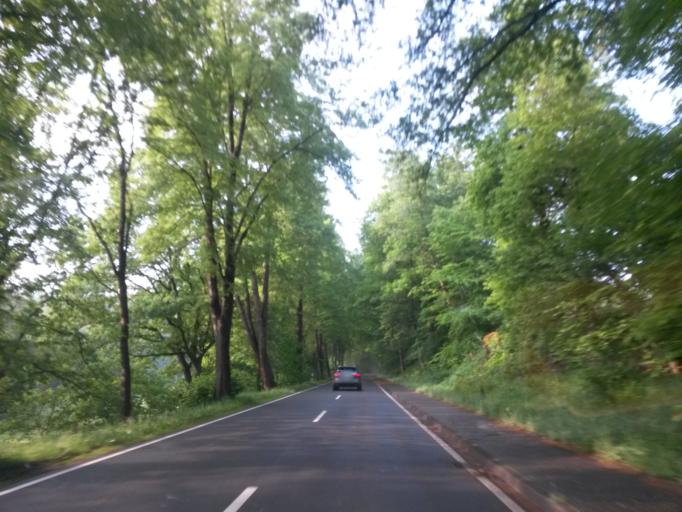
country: DE
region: North Rhine-Westphalia
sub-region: Regierungsbezirk Koln
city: Much
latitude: 50.8950
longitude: 7.4065
